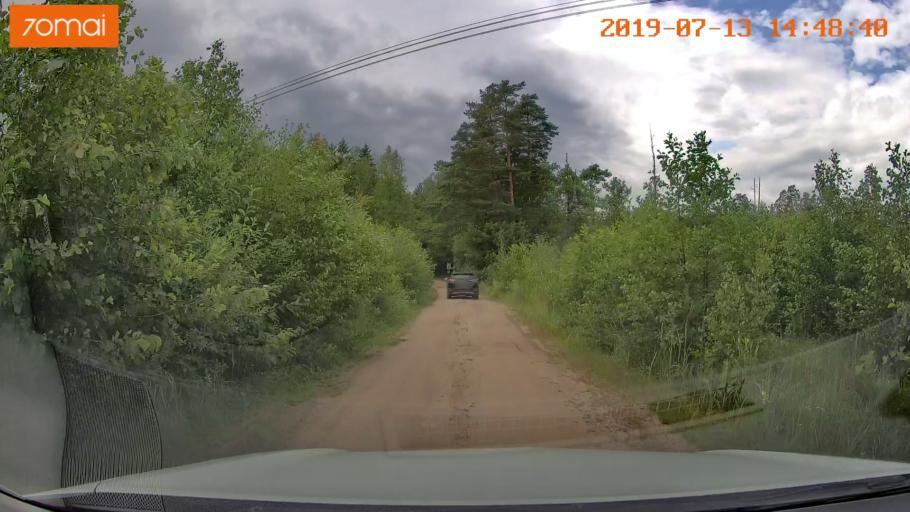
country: BY
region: Mogilev
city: Asipovichy
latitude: 53.2058
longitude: 28.7489
